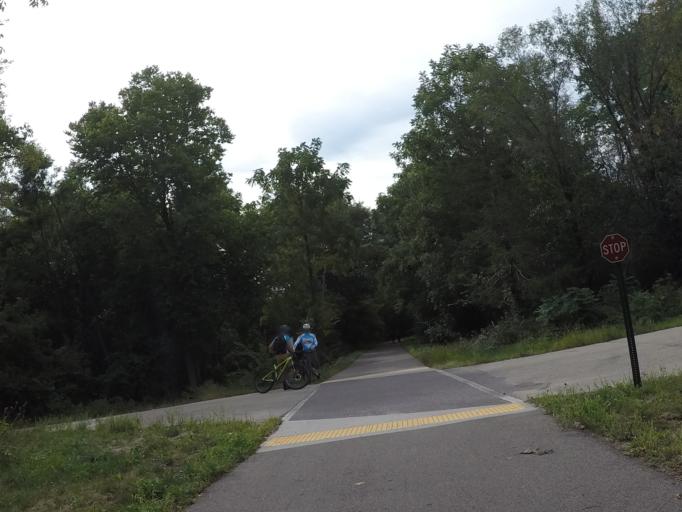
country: US
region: Wisconsin
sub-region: Sauk County
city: Prairie du Sac
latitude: 43.3112
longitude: -89.7331
